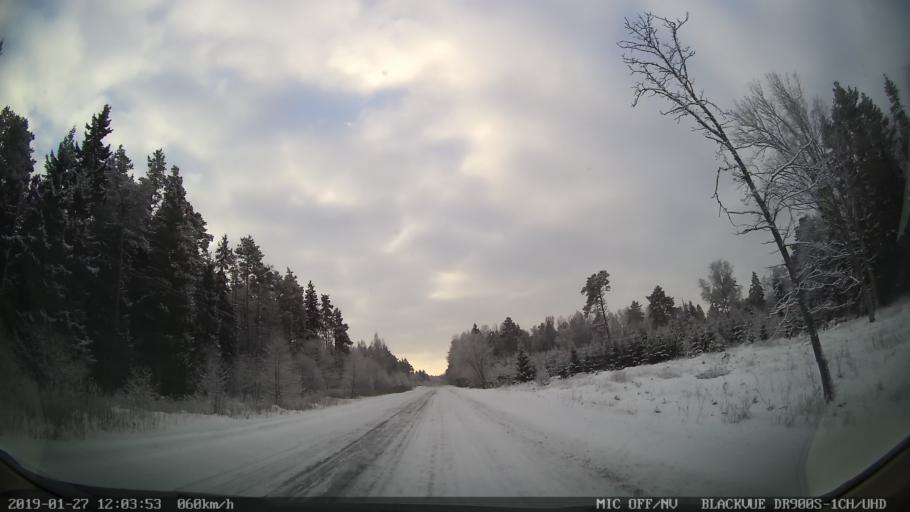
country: EE
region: Harju
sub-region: Raasiku vald
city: Raasiku
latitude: 59.4872
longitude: 25.2608
